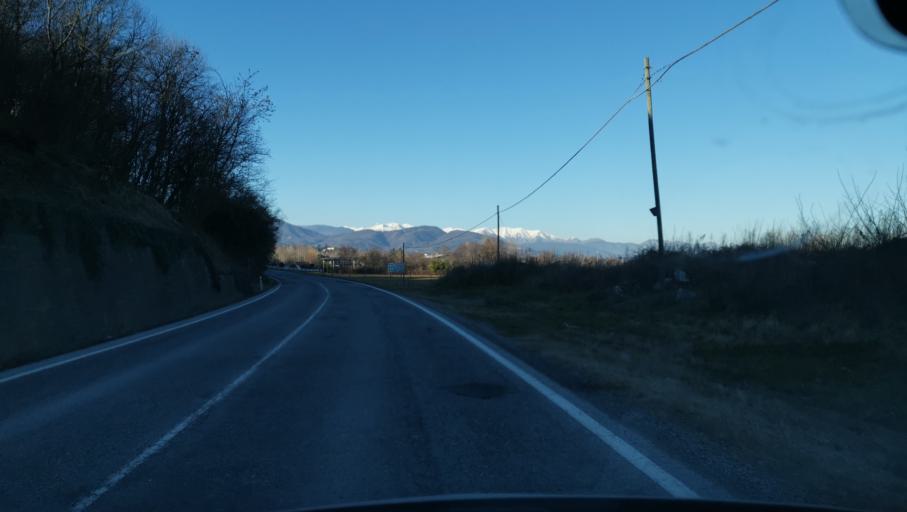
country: IT
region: Piedmont
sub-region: Provincia di Torino
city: Bibiana
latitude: 44.7829
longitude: 7.2989
